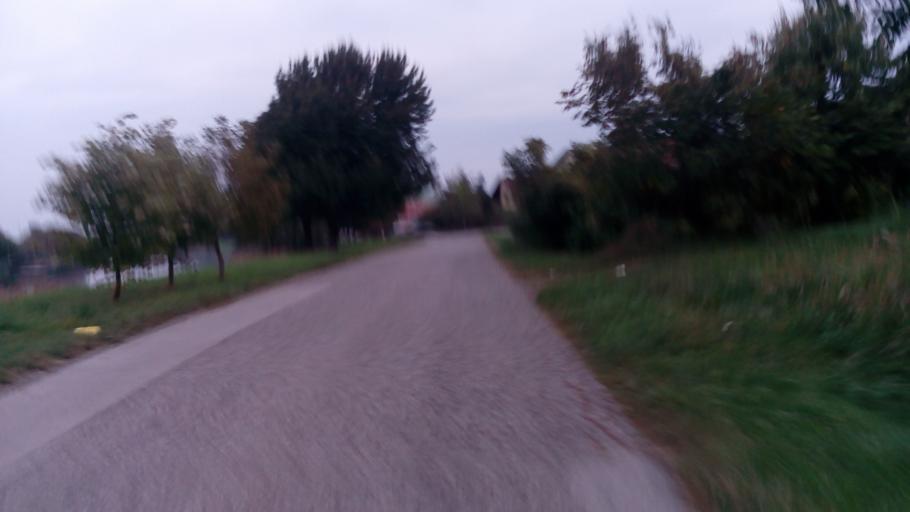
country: HR
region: Vukovarsko-Srijemska
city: Vinkovci
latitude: 45.2773
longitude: 18.8095
